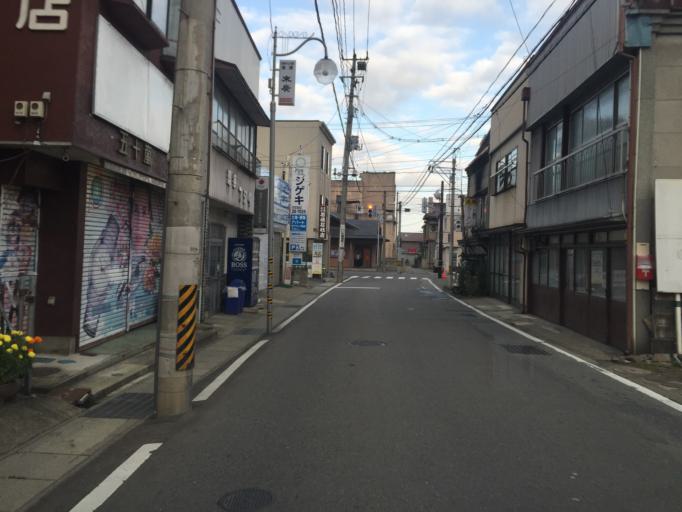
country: JP
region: Fukushima
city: Kitakata
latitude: 37.4957
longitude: 139.9241
